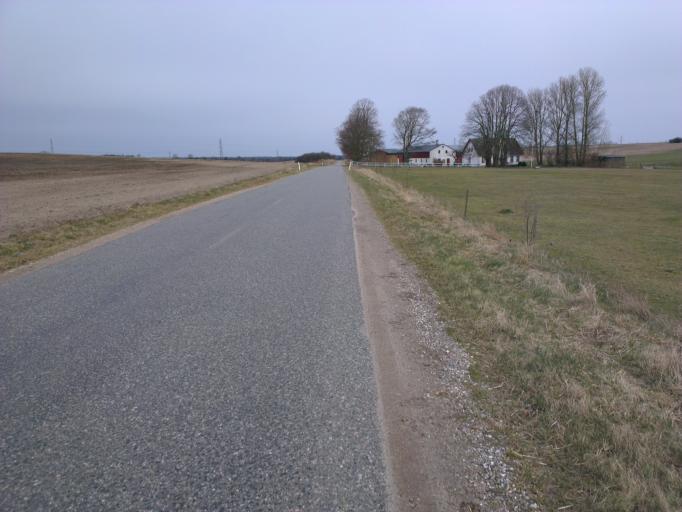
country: DK
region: Capital Region
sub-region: Frederikssund Kommune
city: Skibby
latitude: 55.7970
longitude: 11.9243
